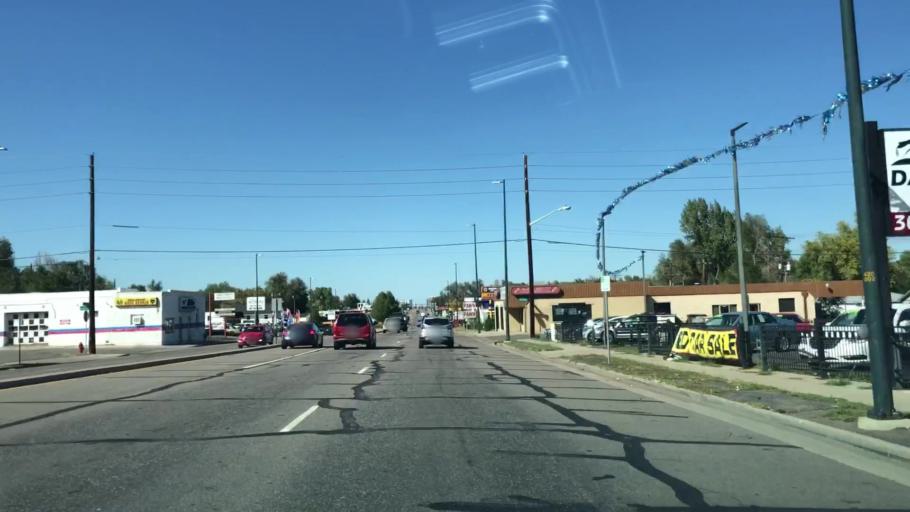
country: US
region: Colorado
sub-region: Arapahoe County
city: Englewood
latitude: 39.6289
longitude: -104.9879
